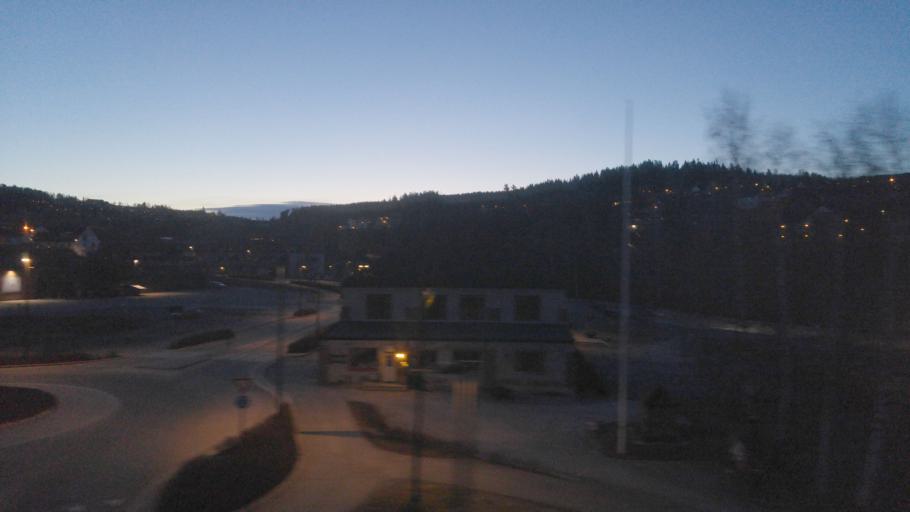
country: NO
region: Hedmark
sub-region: Ringsaker
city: Moelv
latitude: 60.9280
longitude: 10.7008
